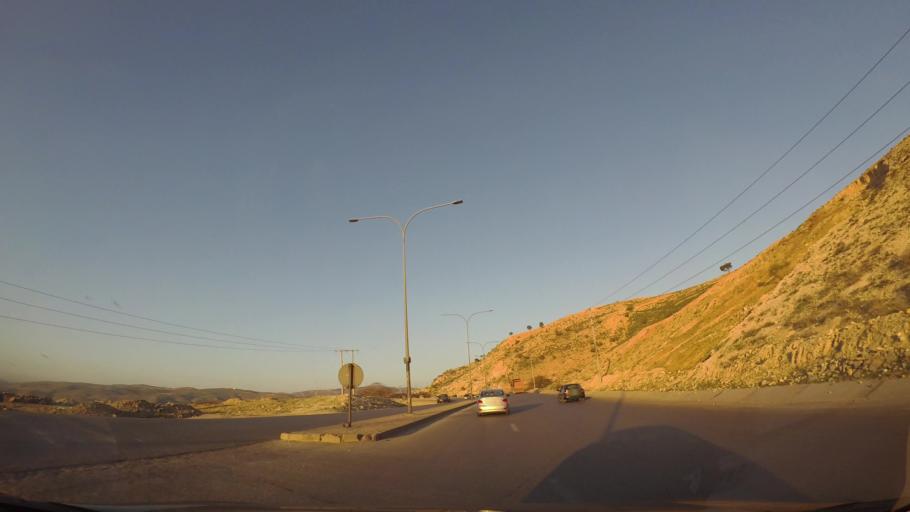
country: JO
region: Balqa
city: Yarqa
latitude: 31.8635
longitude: 35.7220
